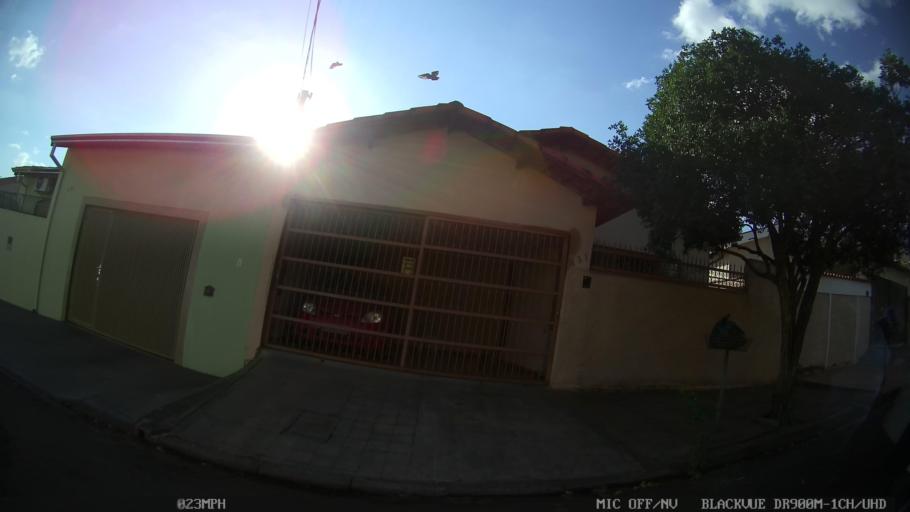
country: BR
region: Sao Paulo
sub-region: Ribeirao Preto
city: Ribeirao Preto
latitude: -21.1893
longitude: -47.7877
